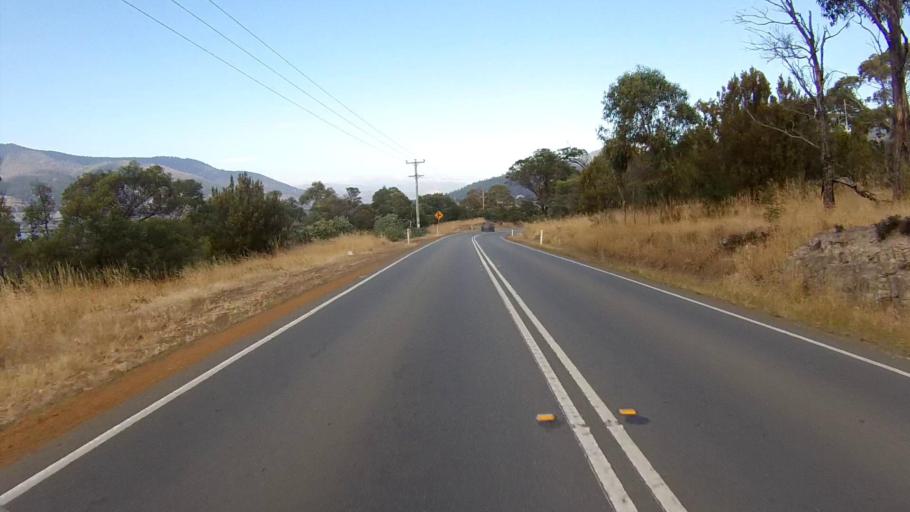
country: AU
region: Tasmania
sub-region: Brighton
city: Bridgewater
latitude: -42.7259
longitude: 147.1949
